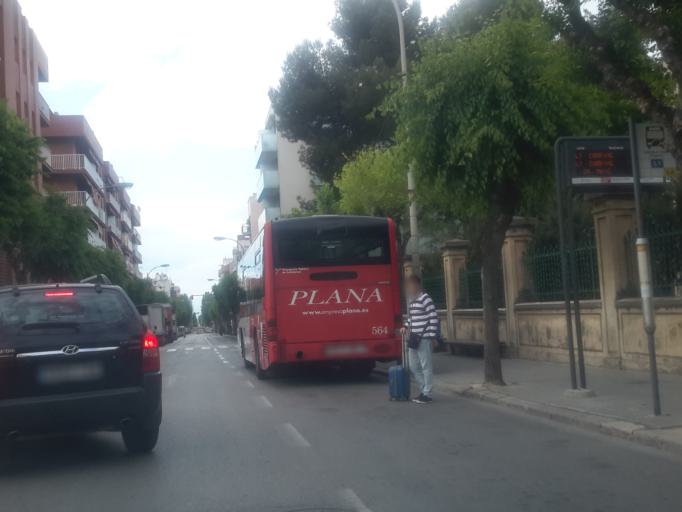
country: ES
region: Catalonia
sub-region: Provincia de Barcelona
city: Vilanova i la Geltru
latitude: 41.2224
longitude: 1.7230
